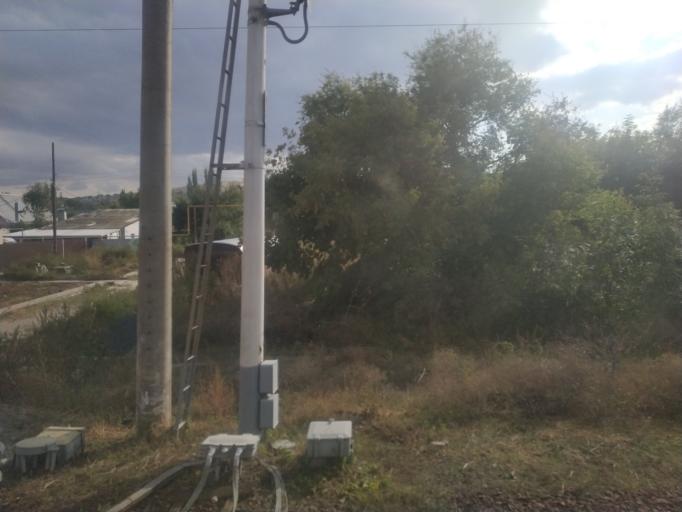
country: RU
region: Volgograd
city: Krasnoslobodsk
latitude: 48.5080
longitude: 44.5413
